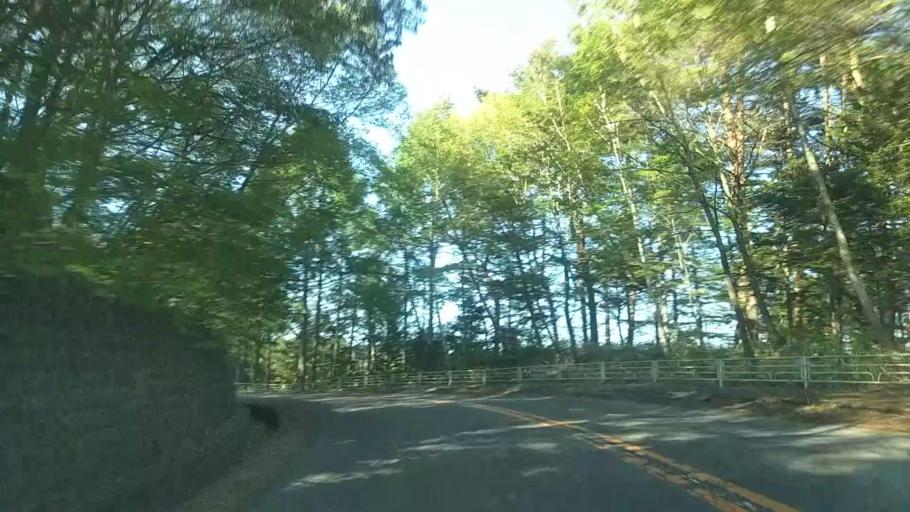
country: JP
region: Yamanashi
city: Nirasaki
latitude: 35.9005
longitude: 138.3744
